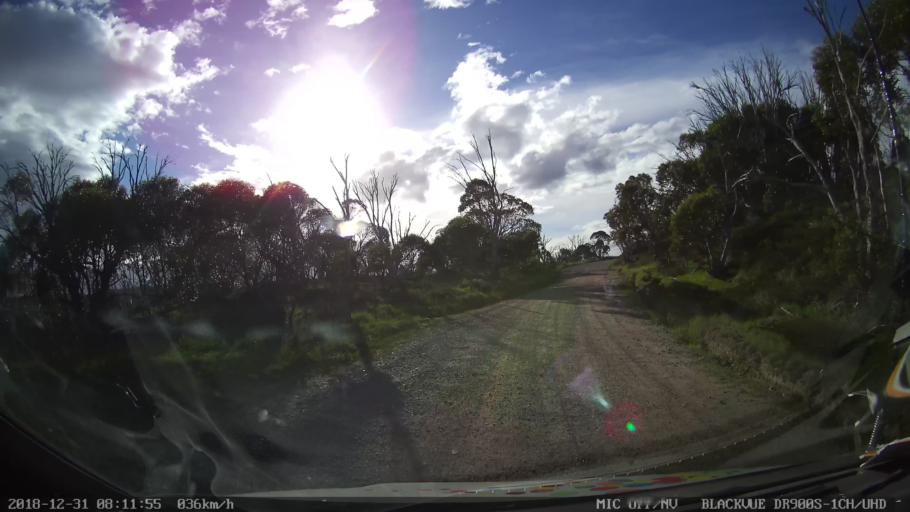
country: AU
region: New South Wales
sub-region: Snowy River
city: Jindabyne
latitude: -36.3855
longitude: 148.4295
